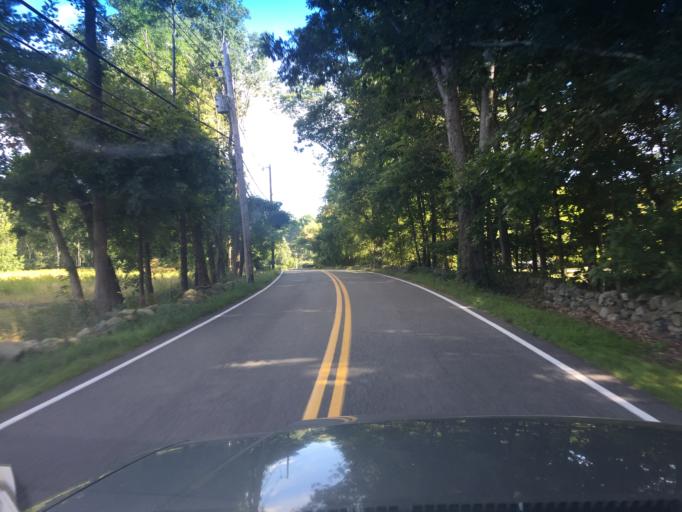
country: US
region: Massachusetts
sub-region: Norfolk County
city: Medfield
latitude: 42.2270
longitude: -71.3262
